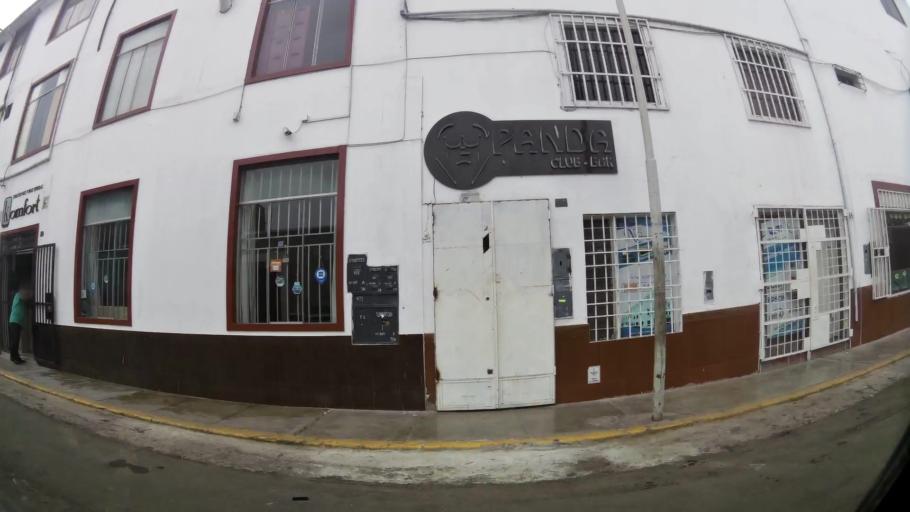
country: PE
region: La Libertad
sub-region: Provincia de Trujillo
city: Trujillo
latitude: -8.1145
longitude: -79.0303
